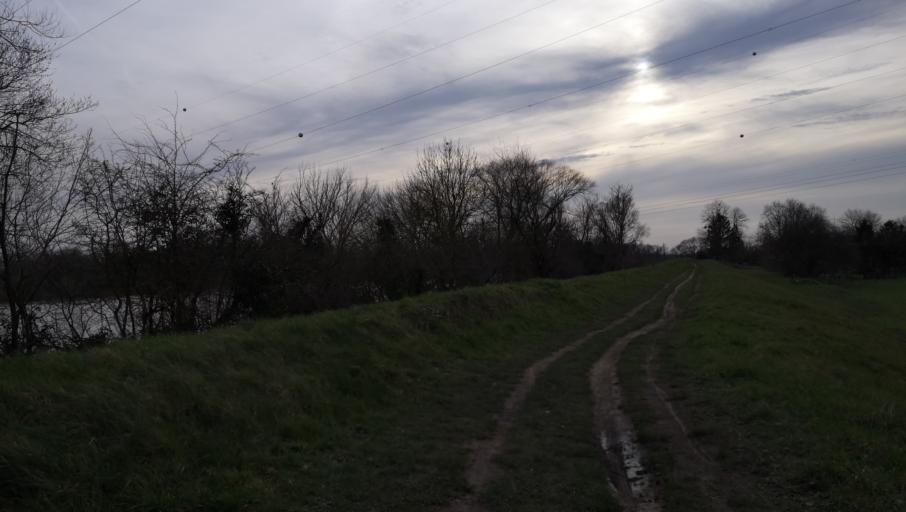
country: FR
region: Centre
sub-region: Departement du Loiret
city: Mareau-aux-Pres
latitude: 47.8685
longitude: 1.8072
